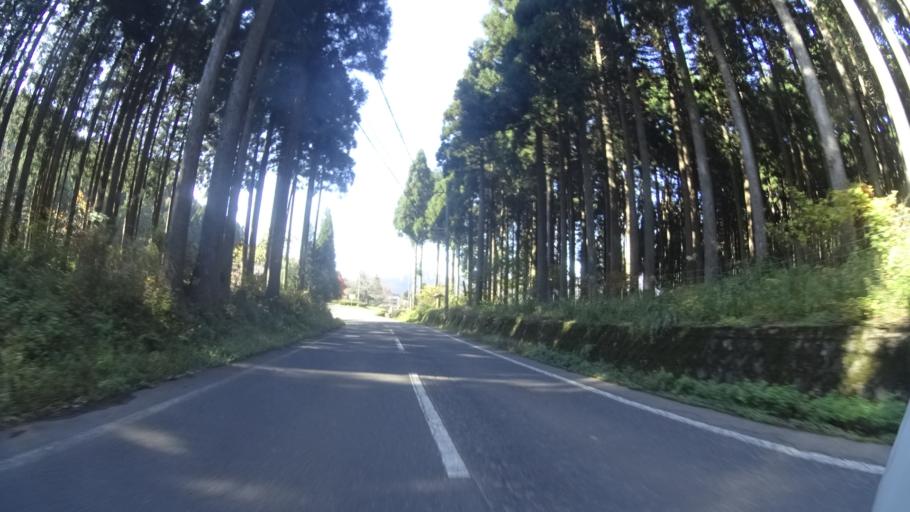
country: JP
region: Fukui
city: Ono
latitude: 35.8774
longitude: 136.3509
